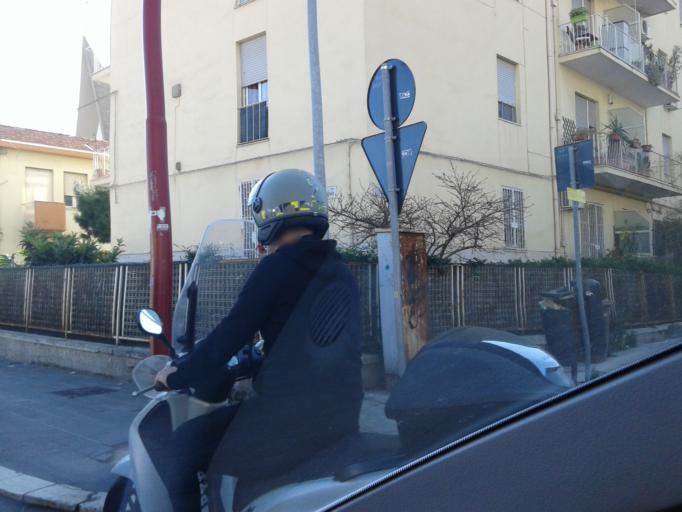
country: IT
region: Sicily
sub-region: Palermo
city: Palermo
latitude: 38.1313
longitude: 13.3406
